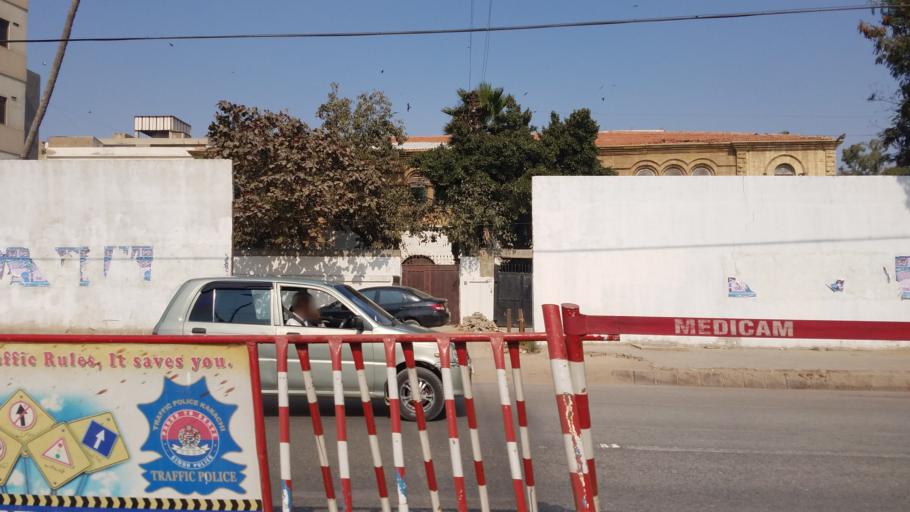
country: PK
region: Sindh
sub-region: Karachi District
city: Karachi
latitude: 24.8500
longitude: 67.0105
